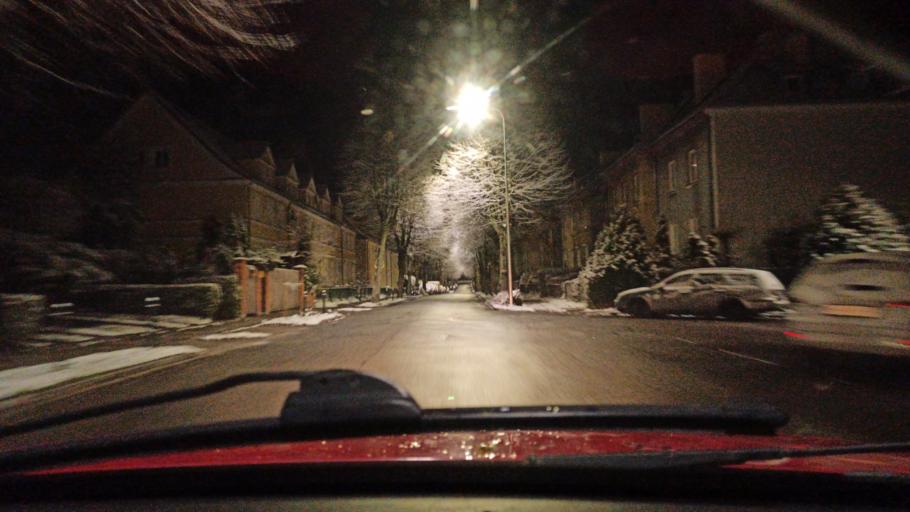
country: PL
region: Warmian-Masurian Voivodeship
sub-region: Powiat elblaski
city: Elblag
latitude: 54.1726
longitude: 19.4080
